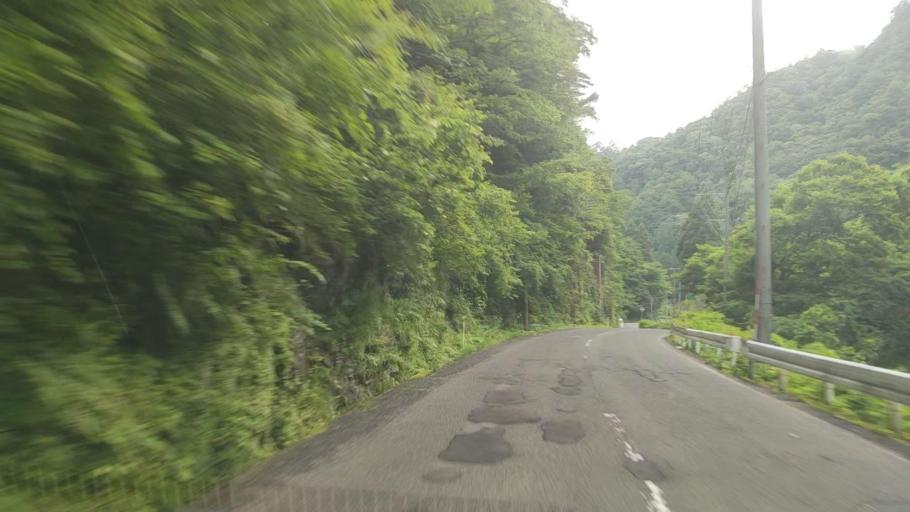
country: JP
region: Tottori
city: Tottori
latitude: 35.3327
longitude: 134.0642
